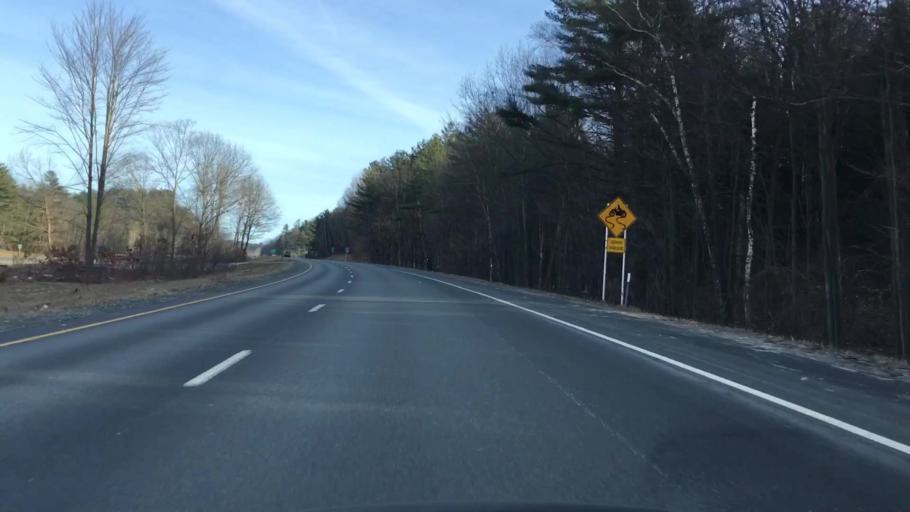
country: US
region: Vermont
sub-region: Windsor County
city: White River Junction
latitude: 43.6308
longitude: -72.3126
